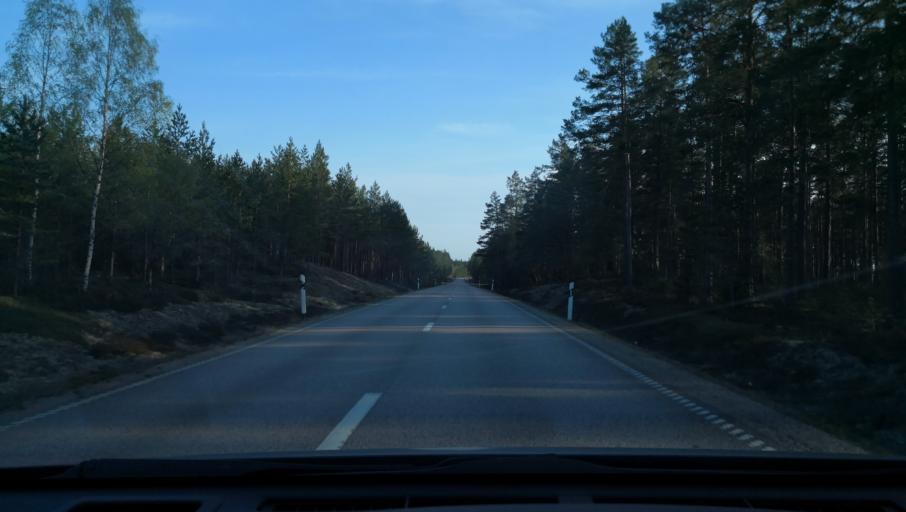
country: SE
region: Uppsala
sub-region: Heby Kommun
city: Heby
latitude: 60.0543
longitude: 16.8658
